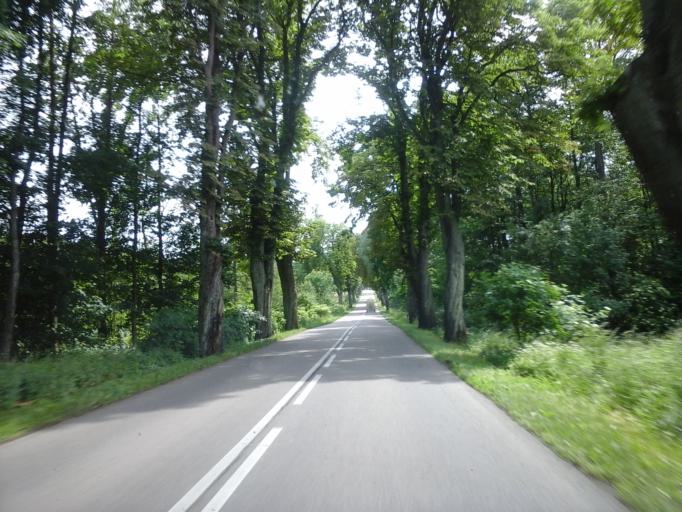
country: PL
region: West Pomeranian Voivodeship
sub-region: Powiat lobeski
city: Lobez
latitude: 53.5896
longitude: 15.5965
